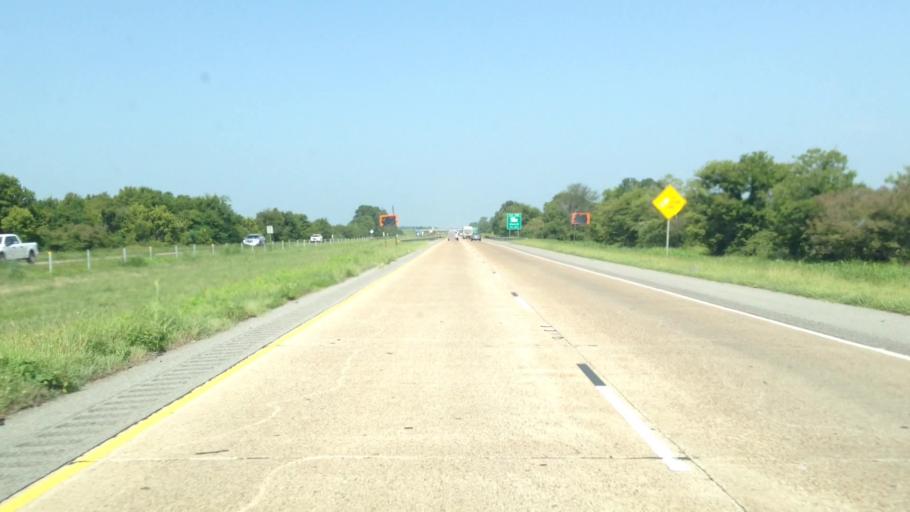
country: US
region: Mississippi
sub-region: Warren County
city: Vicksburg
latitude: 32.3276
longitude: -91.0094
